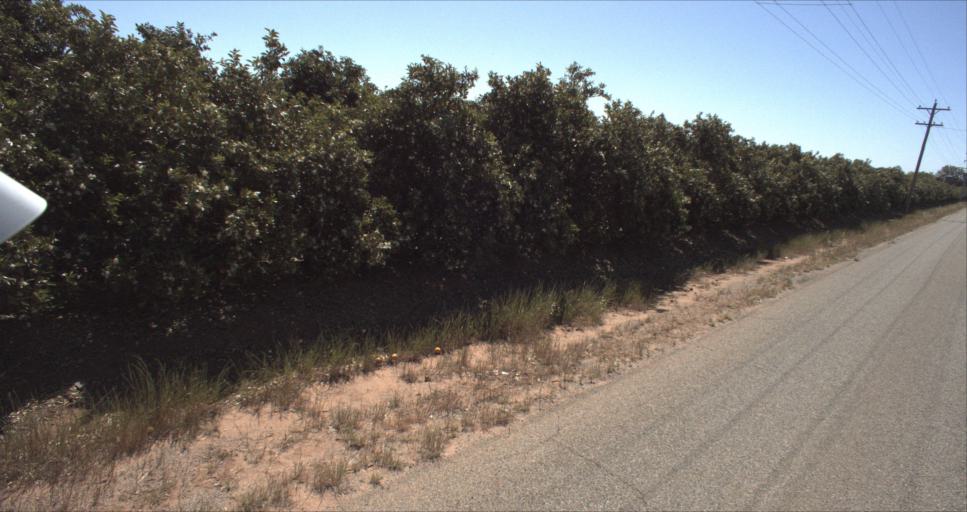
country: AU
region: New South Wales
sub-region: Leeton
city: Leeton
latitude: -34.5363
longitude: 146.3523
